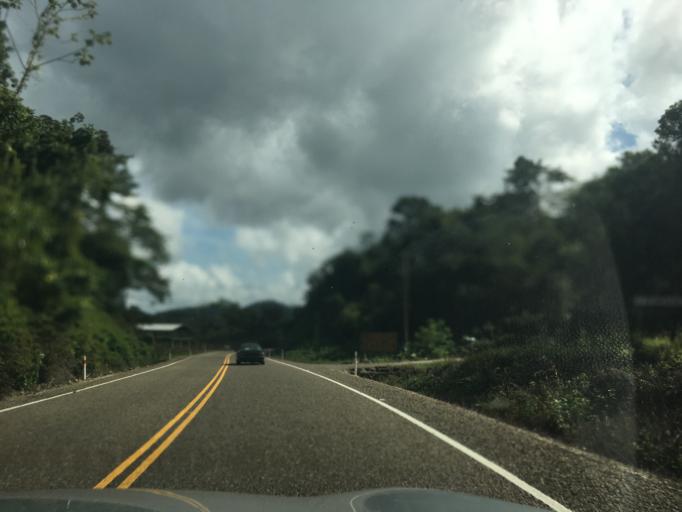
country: BZ
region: Cayo
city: Belmopan
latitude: 17.1494
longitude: -88.7133
